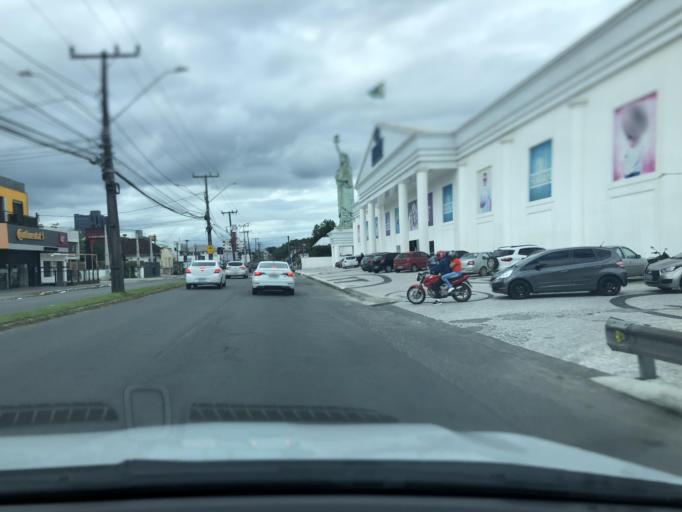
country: BR
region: Santa Catarina
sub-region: Joinville
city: Joinville
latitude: -26.3091
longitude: -48.8408
